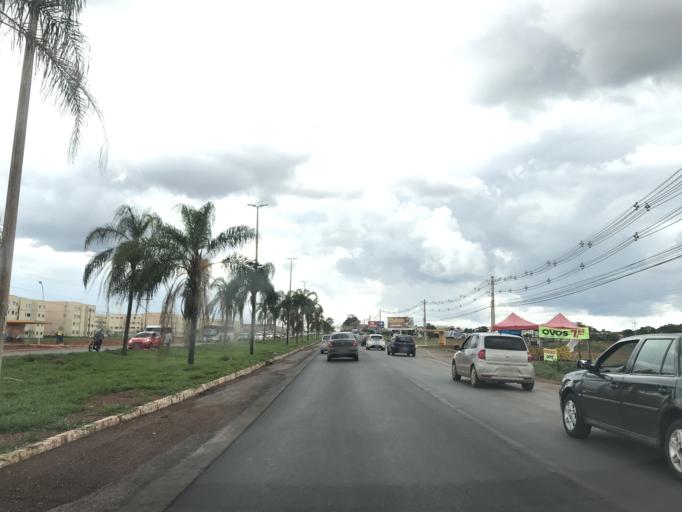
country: BR
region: Federal District
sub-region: Brasilia
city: Brasilia
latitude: -15.8935
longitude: -48.0570
